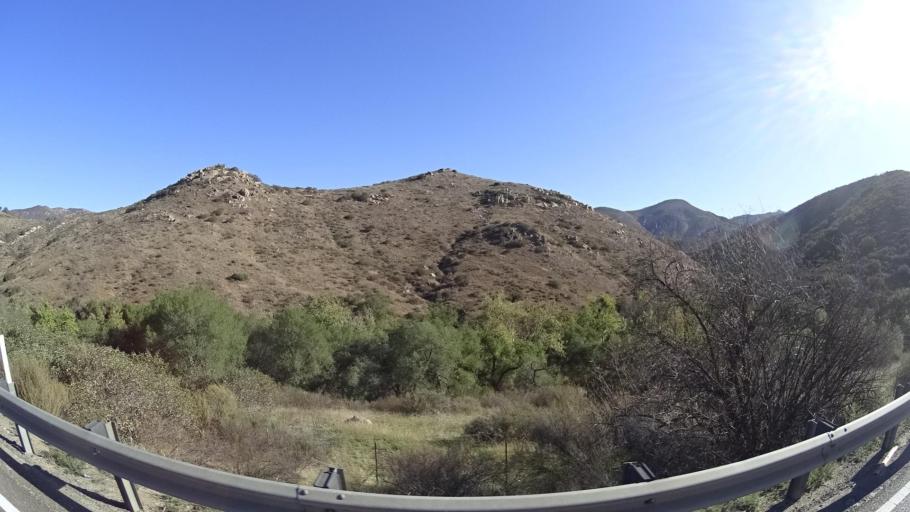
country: US
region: California
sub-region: San Diego County
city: Jamul
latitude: 32.6500
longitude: -116.7871
